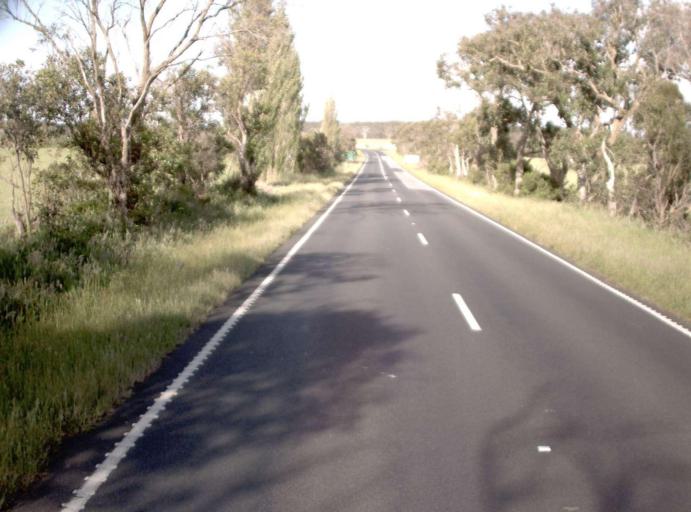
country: AU
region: Victoria
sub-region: Bass Coast
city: North Wonthaggi
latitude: -38.5796
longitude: 145.8257
